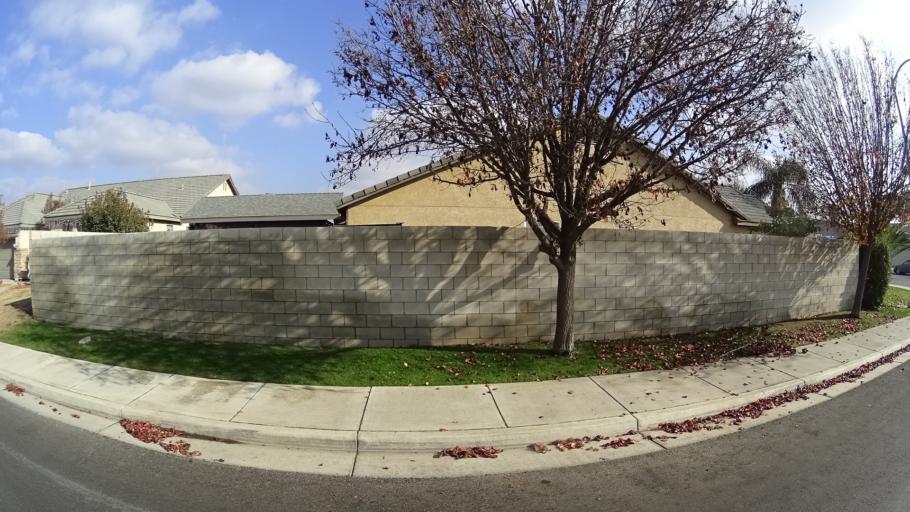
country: US
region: California
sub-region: Kern County
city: Greenacres
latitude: 35.2999
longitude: -119.1048
